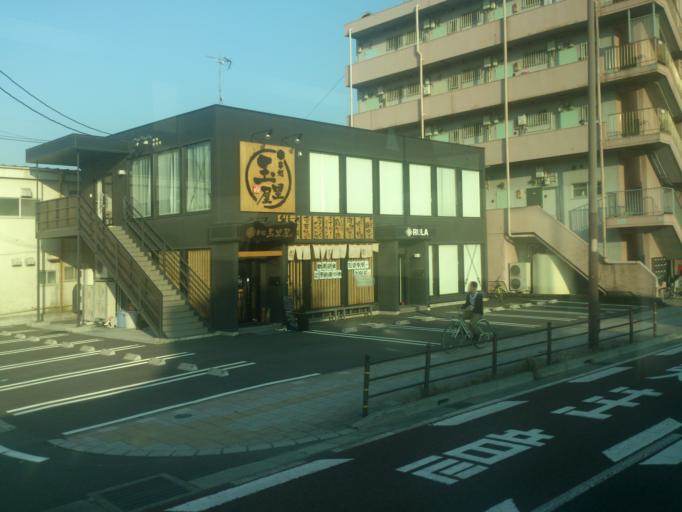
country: JP
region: Kagoshima
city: Kagoshima-shi
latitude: 31.6103
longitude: 130.5340
